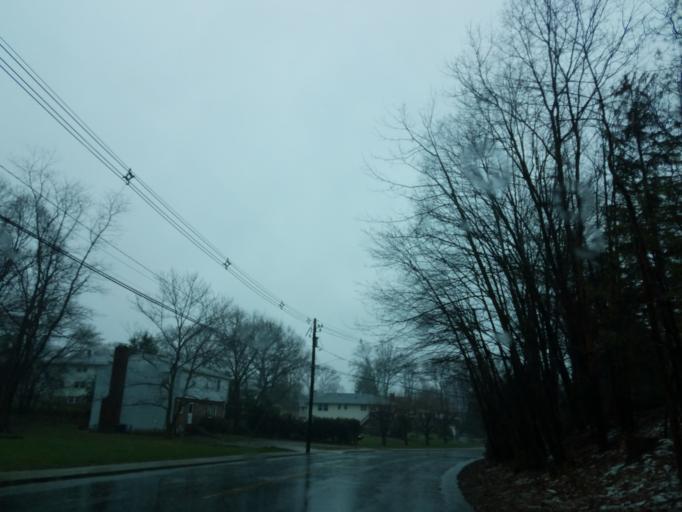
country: US
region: Connecticut
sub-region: New Haven County
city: Waterbury
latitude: 41.5388
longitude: -73.0662
